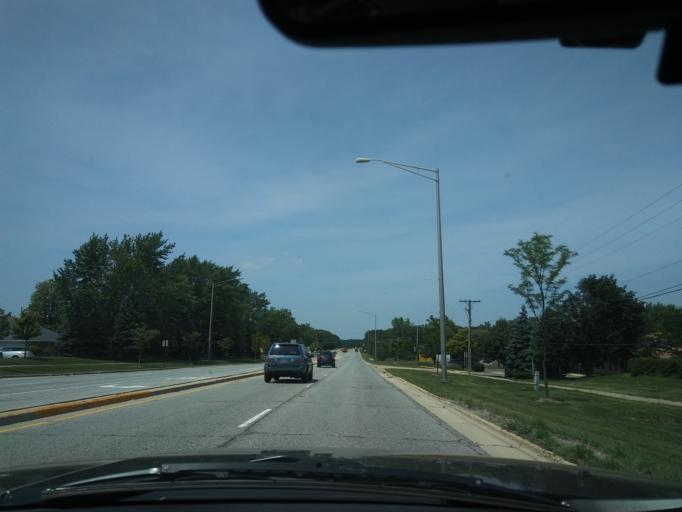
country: US
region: Illinois
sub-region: Cook County
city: Tinley Park
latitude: 41.6135
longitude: -87.7944
